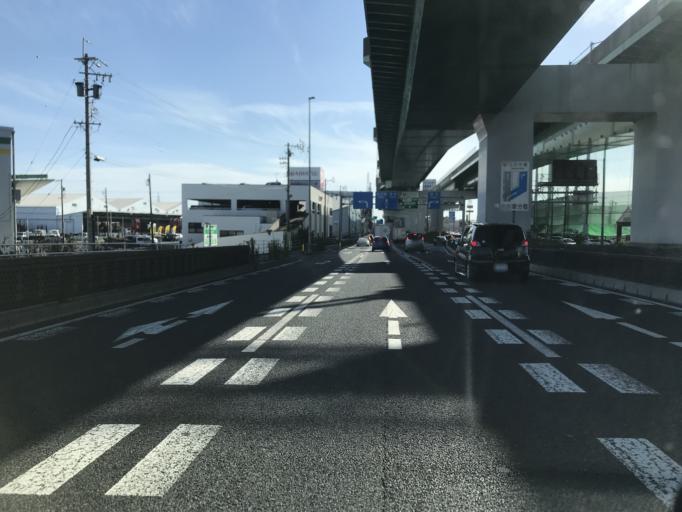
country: JP
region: Aichi
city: Iwakura
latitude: 35.2585
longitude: 136.8424
